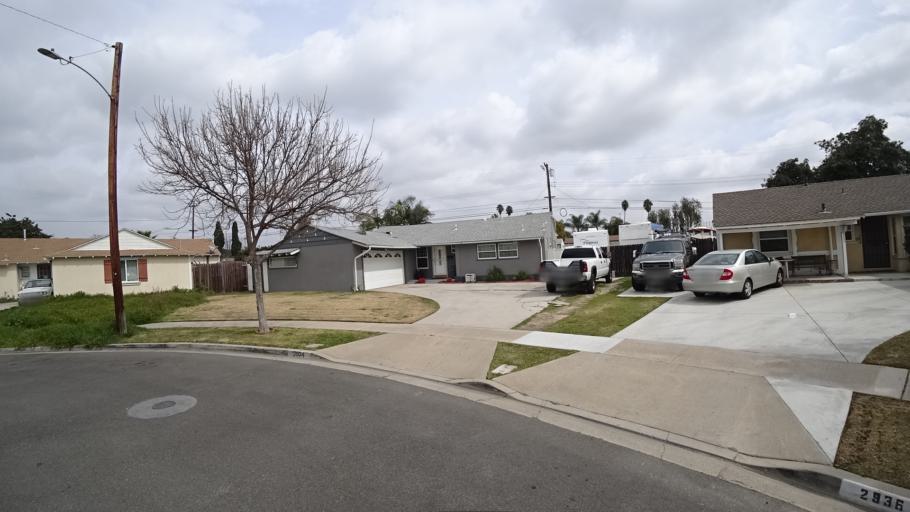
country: US
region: California
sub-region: Orange County
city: Stanton
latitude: 33.8264
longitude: -117.9905
